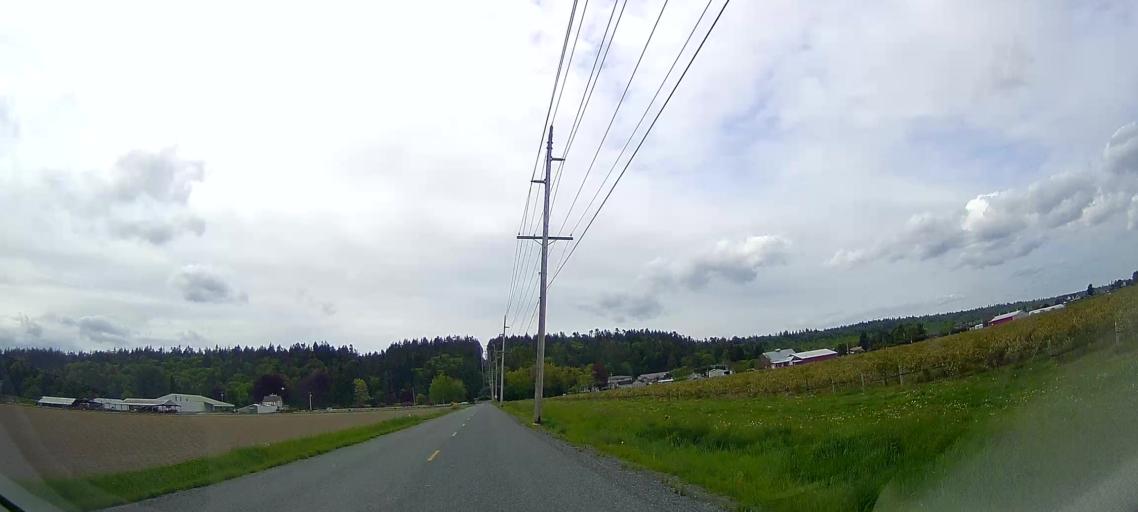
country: US
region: Washington
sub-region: Skagit County
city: Anacortes
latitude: 48.4210
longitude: -122.4937
